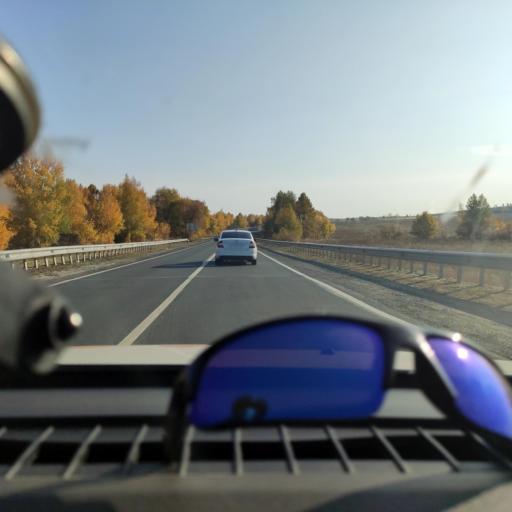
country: RU
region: Samara
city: Bereza
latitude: 53.4851
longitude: 50.1167
